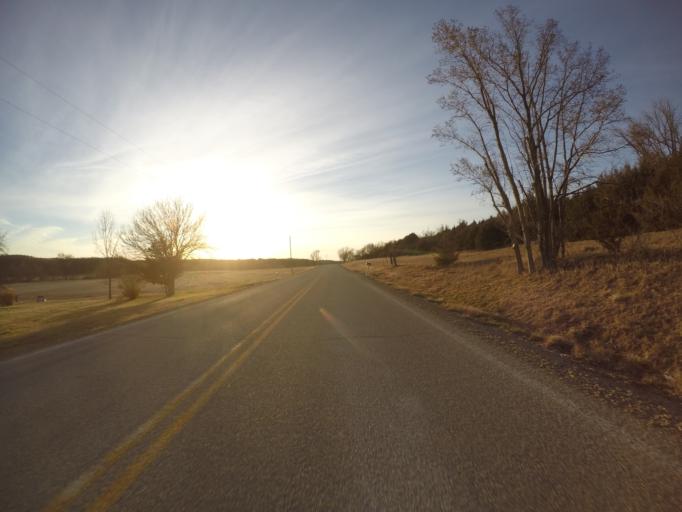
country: US
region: Kansas
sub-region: Riley County
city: Ogden
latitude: 39.3058
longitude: -96.7253
